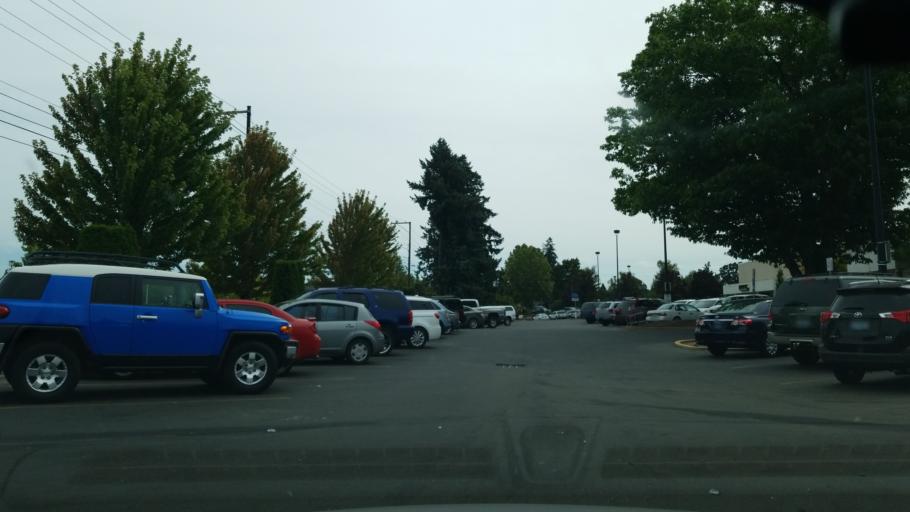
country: US
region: Oregon
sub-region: Clackamas County
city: Clackamas
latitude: 45.4051
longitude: -122.5692
